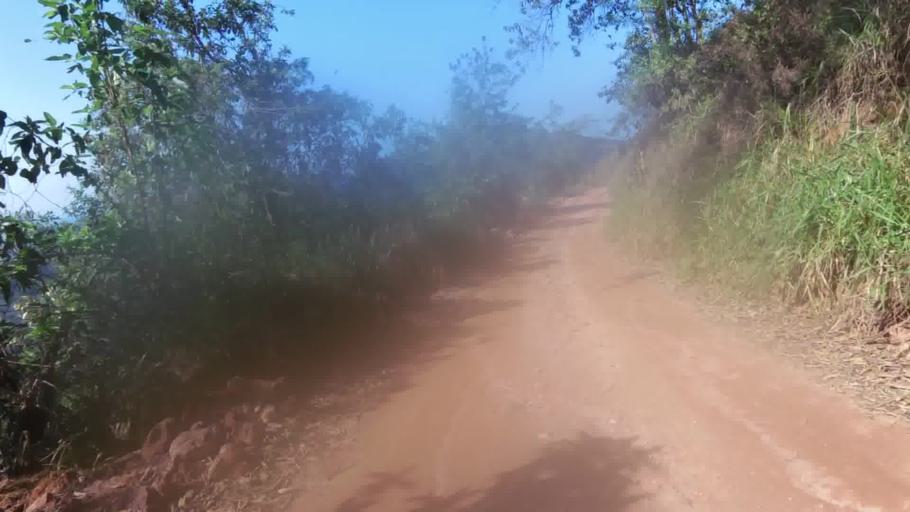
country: BR
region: Espirito Santo
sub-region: Alfredo Chaves
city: Alfredo Chaves
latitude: -20.6788
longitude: -40.7820
